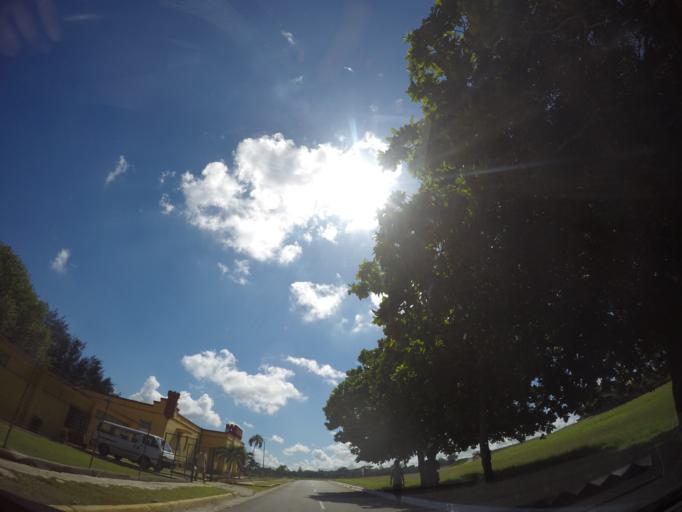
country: CU
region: La Habana
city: Centro Habana
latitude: 23.1490
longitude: -82.3489
